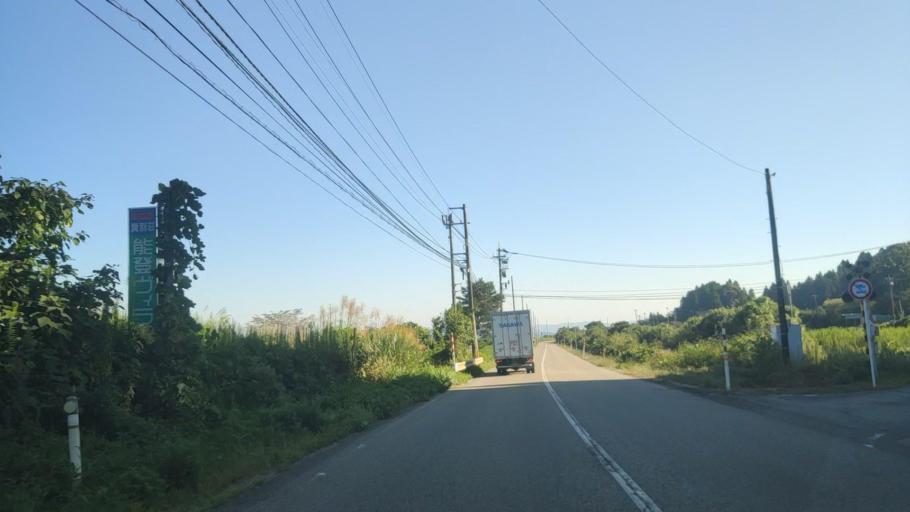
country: JP
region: Ishikawa
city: Nanao
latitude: 37.1983
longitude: 136.9098
